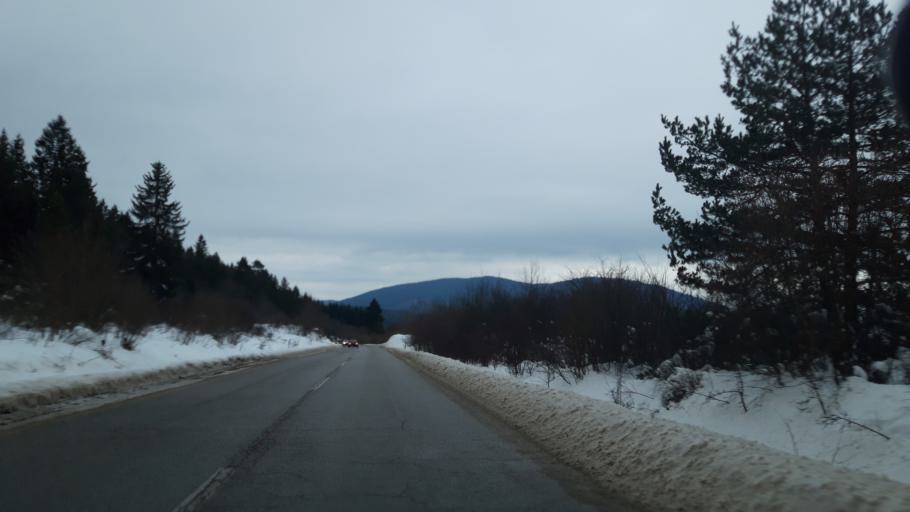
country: BA
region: Republika Srpska
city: Han Pijesak
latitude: 44.0223
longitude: 18.8822
